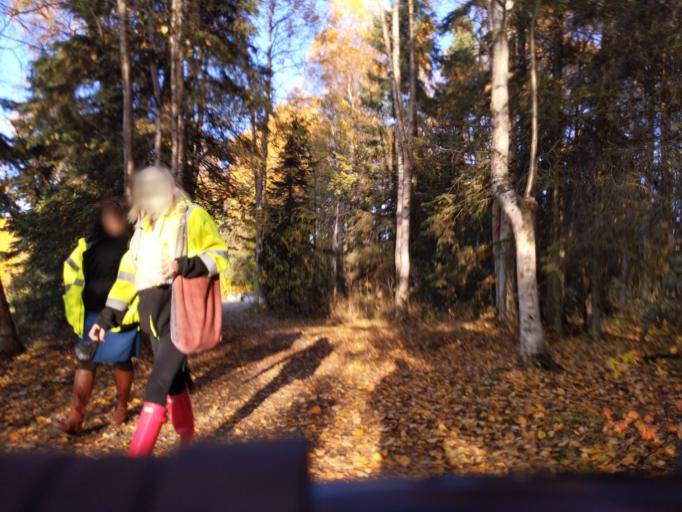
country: US
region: Alaska
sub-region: Anchorage Municipality
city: Anchorage
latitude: 61.1493
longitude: -149.8805
